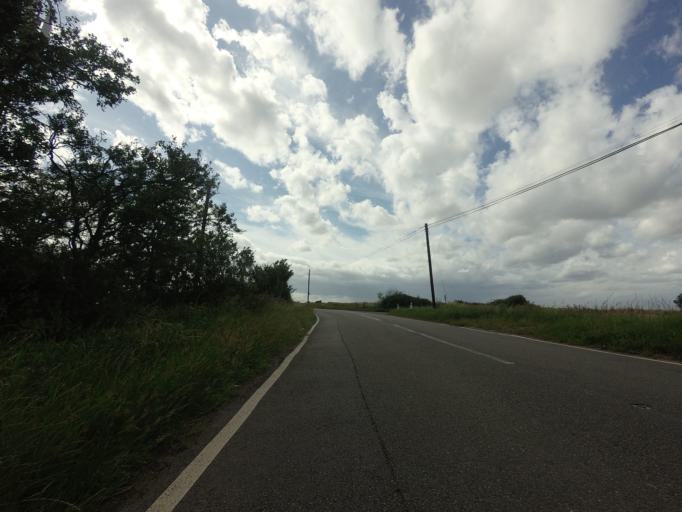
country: GB
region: England
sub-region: Medway
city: Allhallows
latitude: 51.4677
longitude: 0.6301
